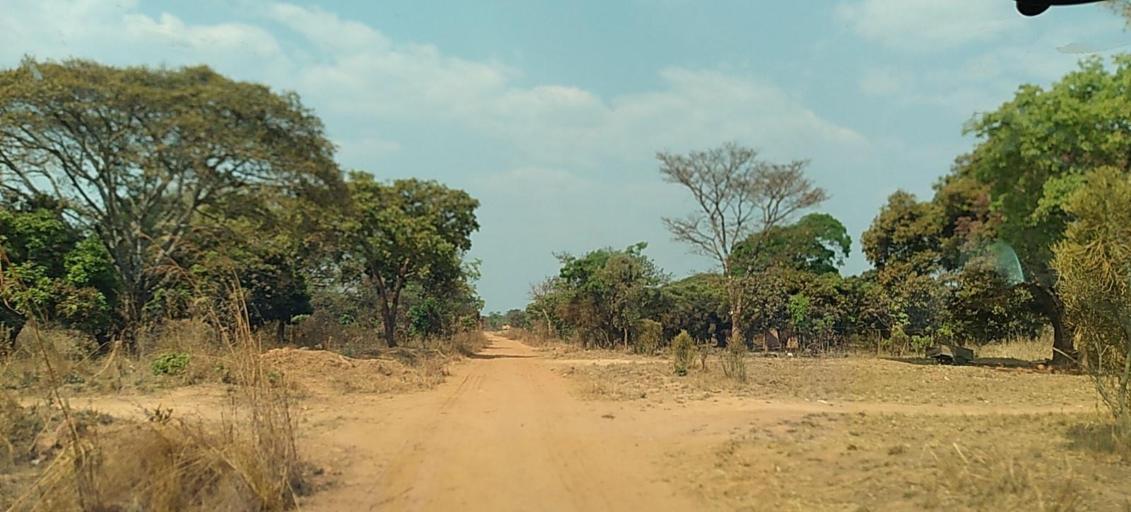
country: ZM
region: North-Western
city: Kasempa
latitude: -13.3054
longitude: 26.0747
